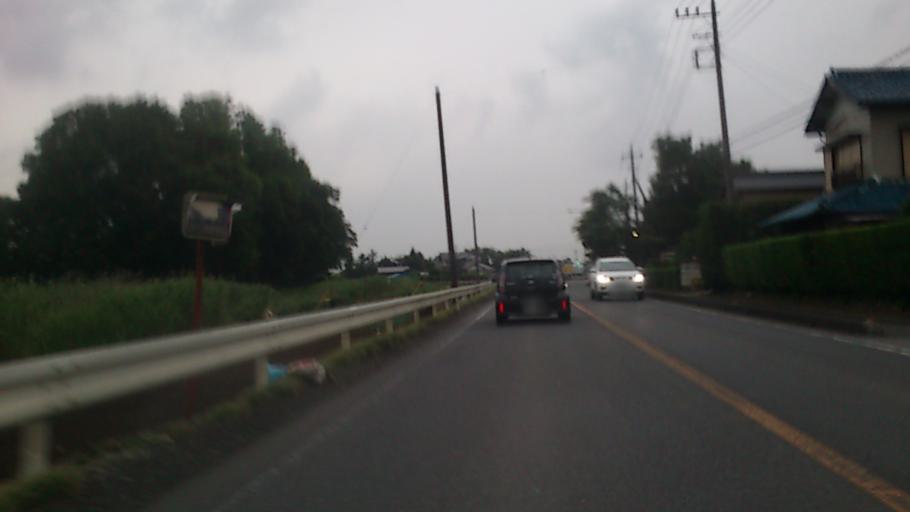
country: JP
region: Saitama
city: Kazo
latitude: 36.1615
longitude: 139.6017
